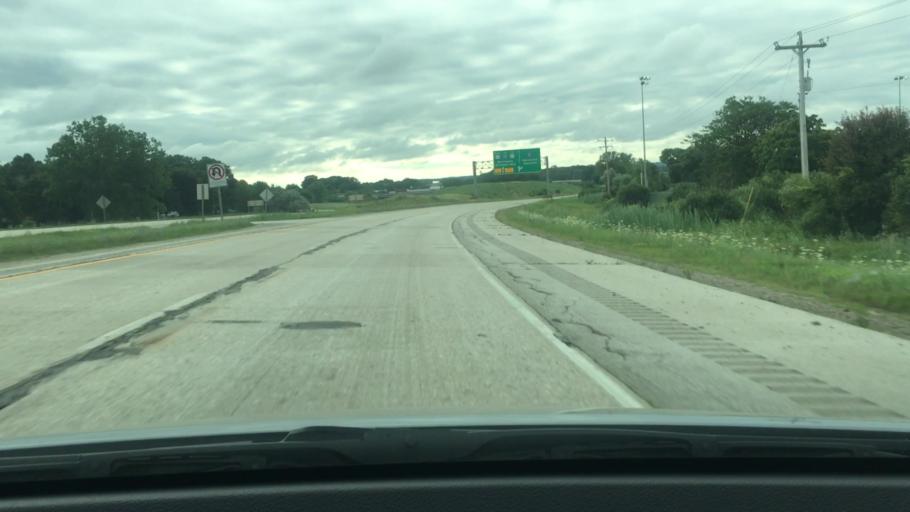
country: US
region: Wisconsin
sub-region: Brown County
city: Ashwaubenon
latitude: 44.4897
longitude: -88.0908
